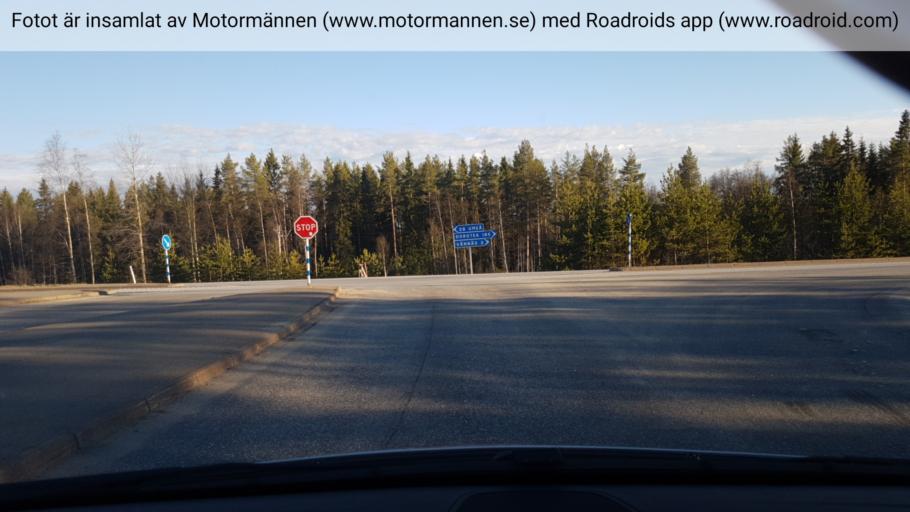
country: SE
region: Vaesterbotten
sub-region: Vannas Kommun
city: Vaennaes
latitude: 63.9229
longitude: 19.7810
